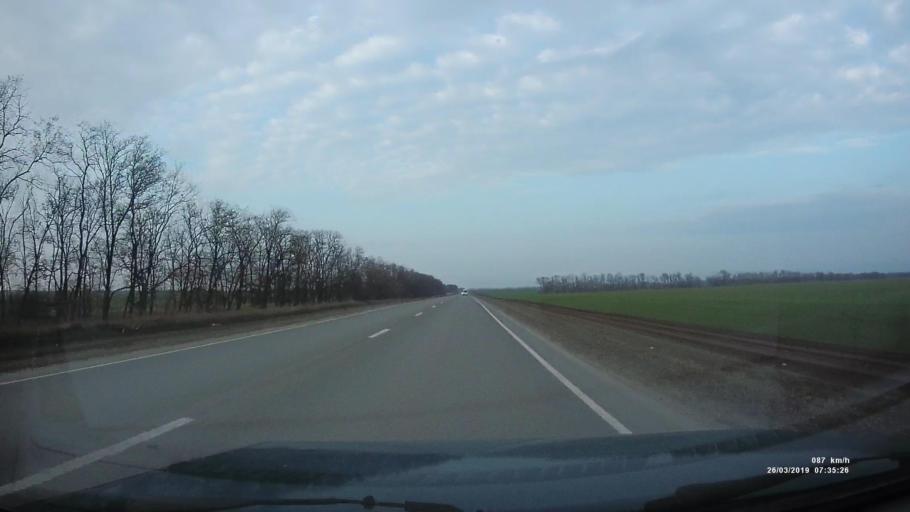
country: RU
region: Rostov
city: Novobessergenovka
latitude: 47.2084
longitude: 38.7376
